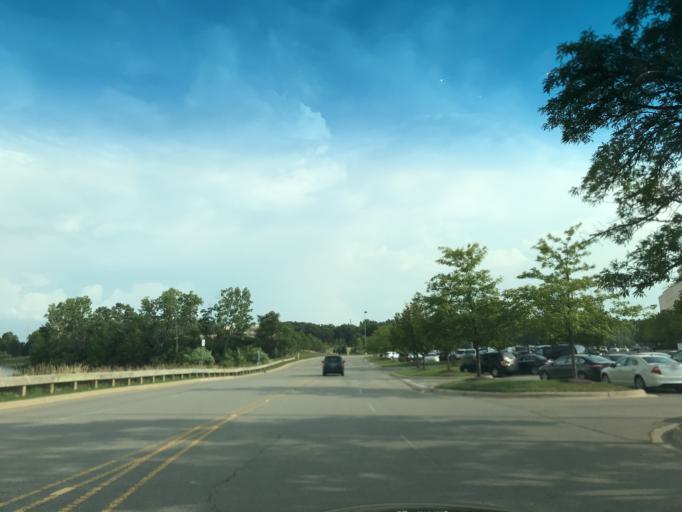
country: US
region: Michigan
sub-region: Oakland County
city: Novi
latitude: 42.4929
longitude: -83.4663
